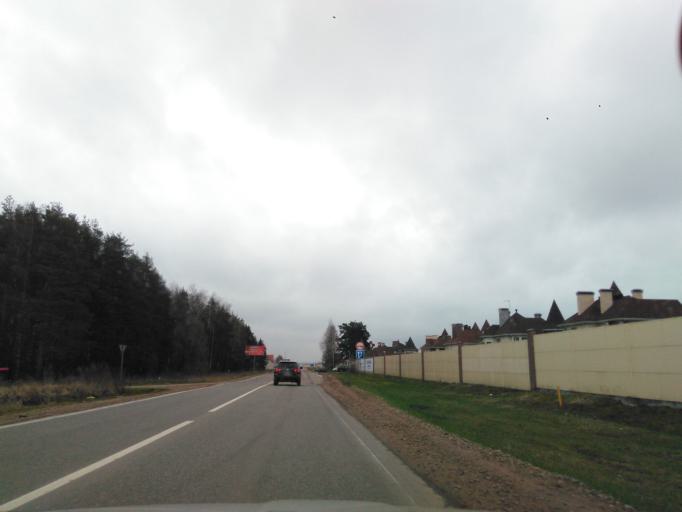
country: RU
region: Moskovskaya
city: Rozhdestveno
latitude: 55.8267
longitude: 37.0395
